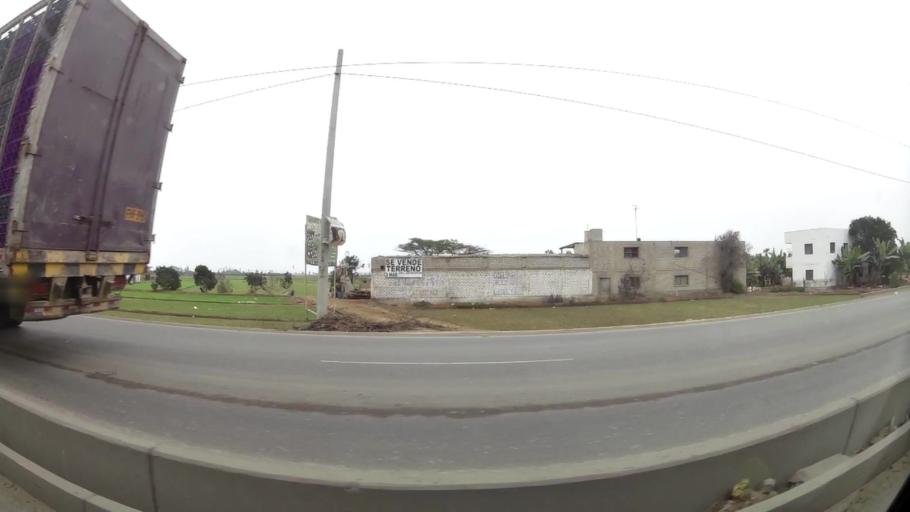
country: PE
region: Lima
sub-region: Lima
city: Punta Hermosa
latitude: -12.2797
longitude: -76.8675
